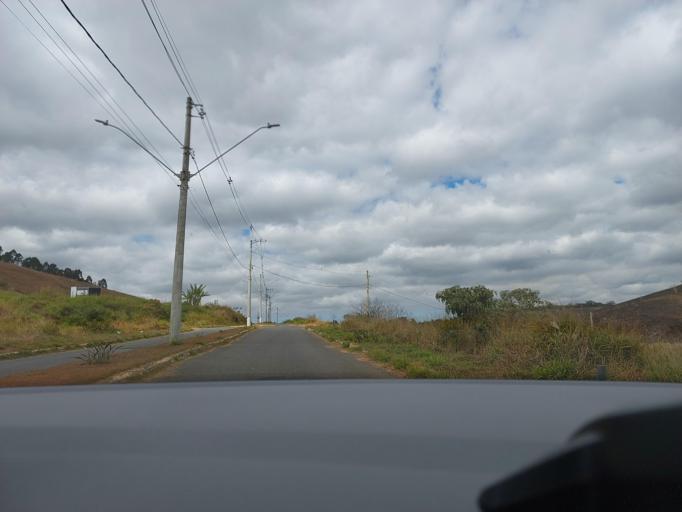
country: BR
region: Minas Gerais
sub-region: Vicosa
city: Vicosa
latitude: -20.7854
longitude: -42.8394
